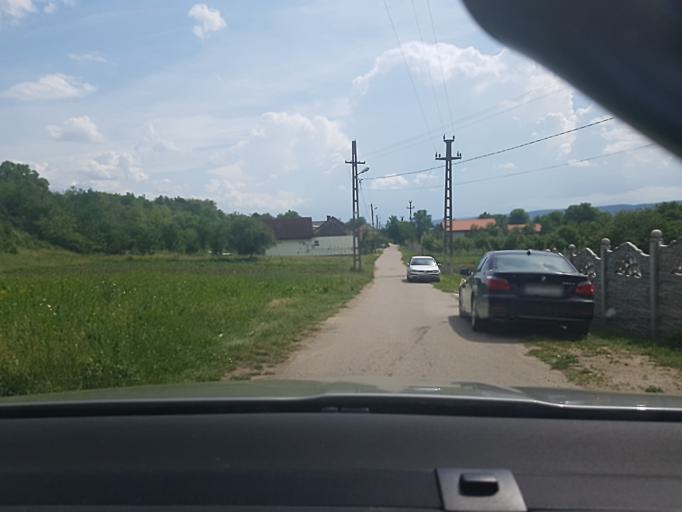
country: RO
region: Hunedoara
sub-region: Comuna Calan
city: Calan
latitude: 45.7213
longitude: 23.0183
